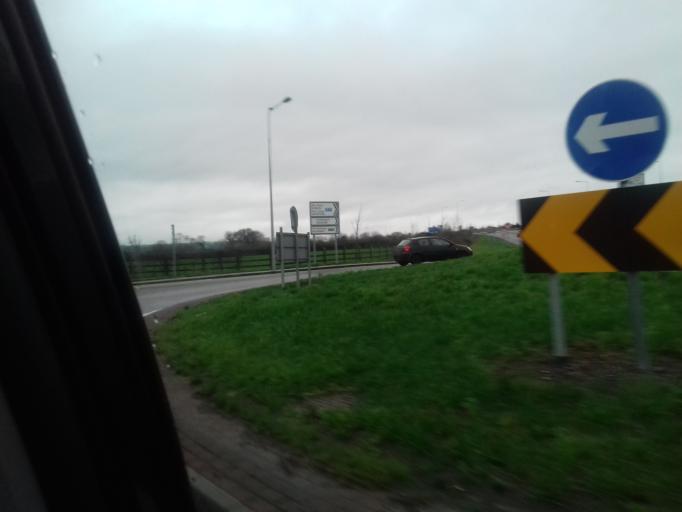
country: IE
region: Leinster
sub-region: County Carlow
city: Bagenalstown
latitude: 52.6788
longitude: -7.0332
